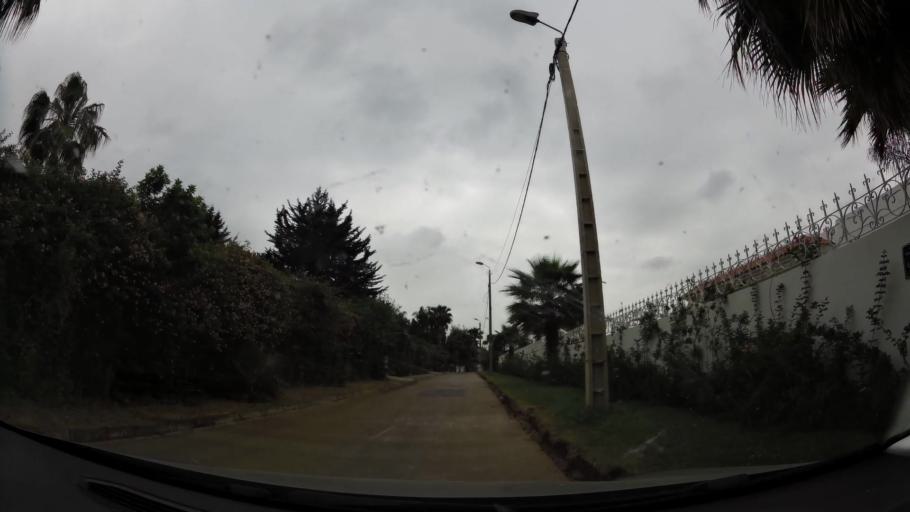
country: MA
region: Rabat-Sale-Zemmour-Zaer
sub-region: Rabat
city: Rabat
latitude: 33.9644
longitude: -6.8144
